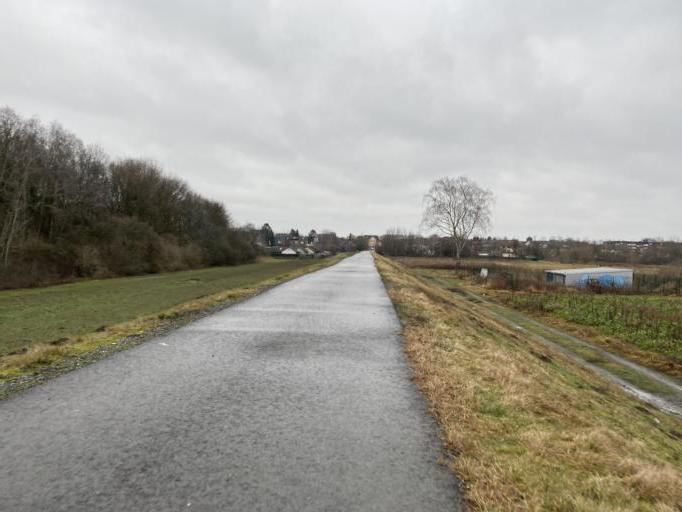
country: DE
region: North Rhine-Westphalia
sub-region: Regierungsbezirk Arnsberg
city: Hamm
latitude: 51.6833
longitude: 7.7879
